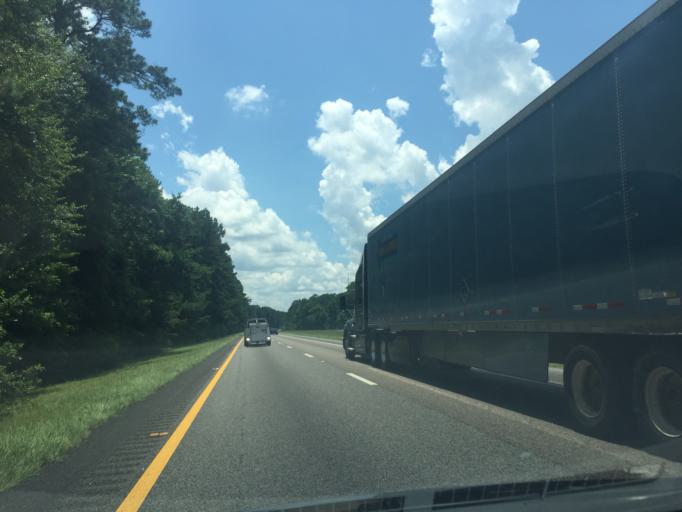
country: US
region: South Carolina
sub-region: Jasper County
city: Hardeeville
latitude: 32.2606
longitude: -81.0957
